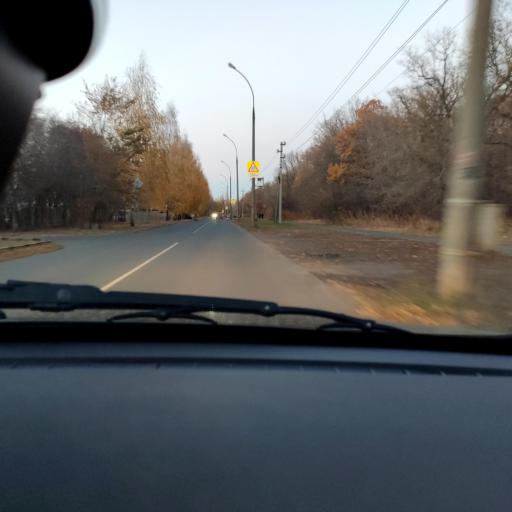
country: RU
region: Samara
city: Tol'yatti
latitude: 53.5088
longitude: 49.3075
